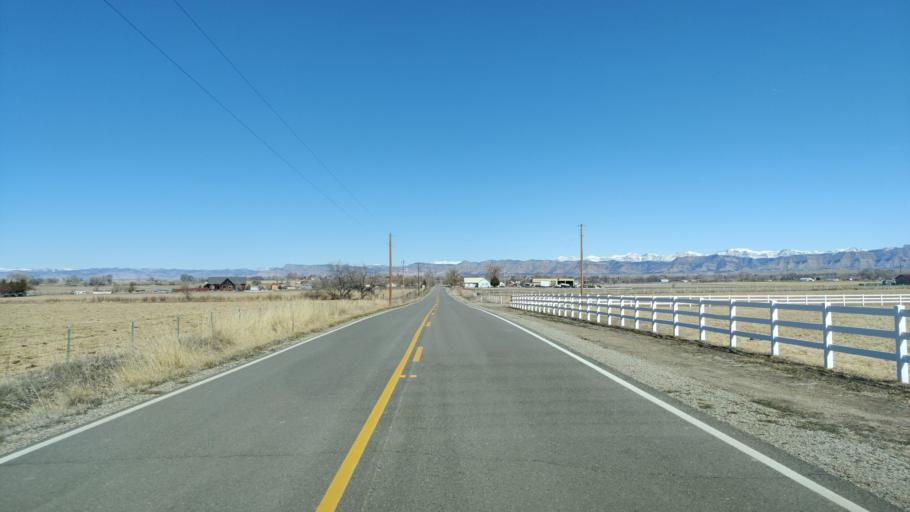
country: US
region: Colorado
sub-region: Mesa County
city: Fruita
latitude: 39.1844
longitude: -108.7105
